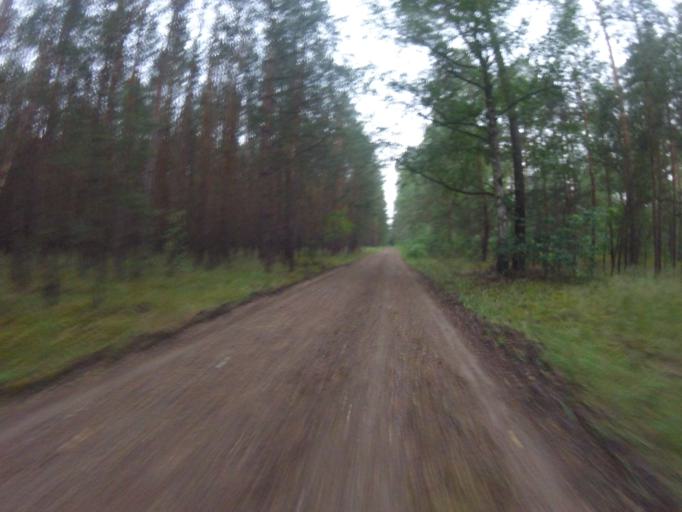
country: DE
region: Brandenburg
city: Gross Koris
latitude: 52.2002
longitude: 13.6967
